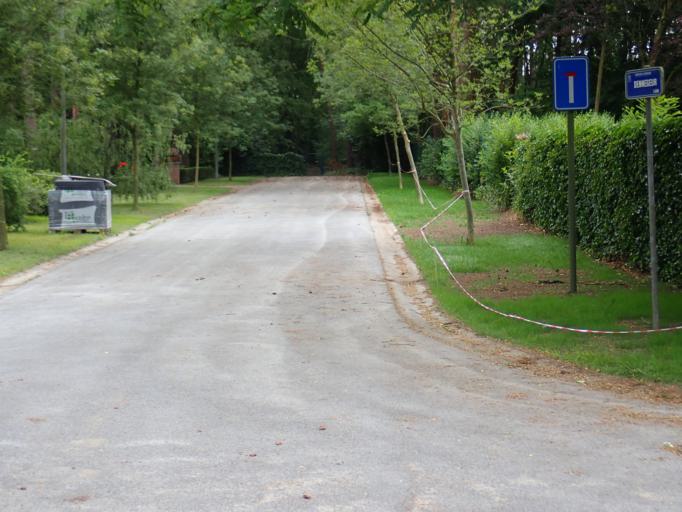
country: BE
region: Flanders
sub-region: Provincie Vlaams-Brabant
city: Boortmeerbeek
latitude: 51.0072
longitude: 4.5907
